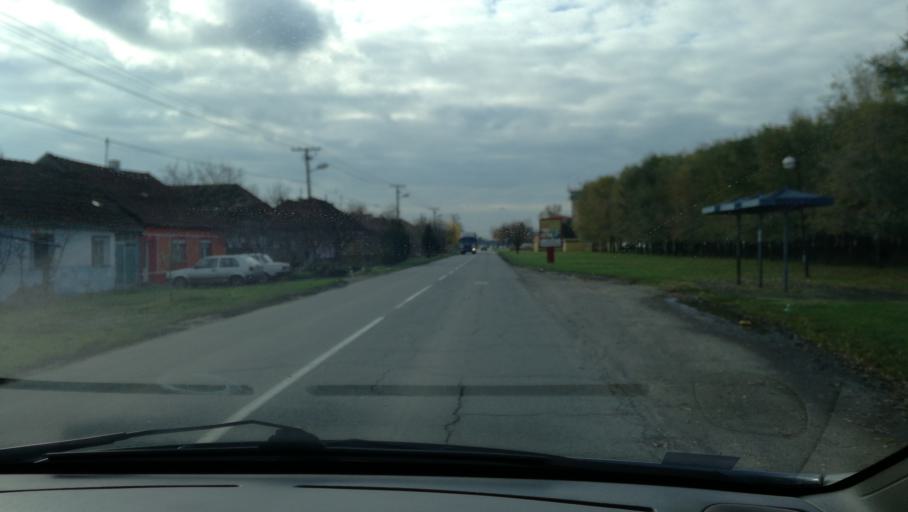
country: RS
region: Autonomna Pokrajina Vojvodina
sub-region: Severnobanatski Okrug
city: Kikinda
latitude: 45.8370
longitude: 20.4515
